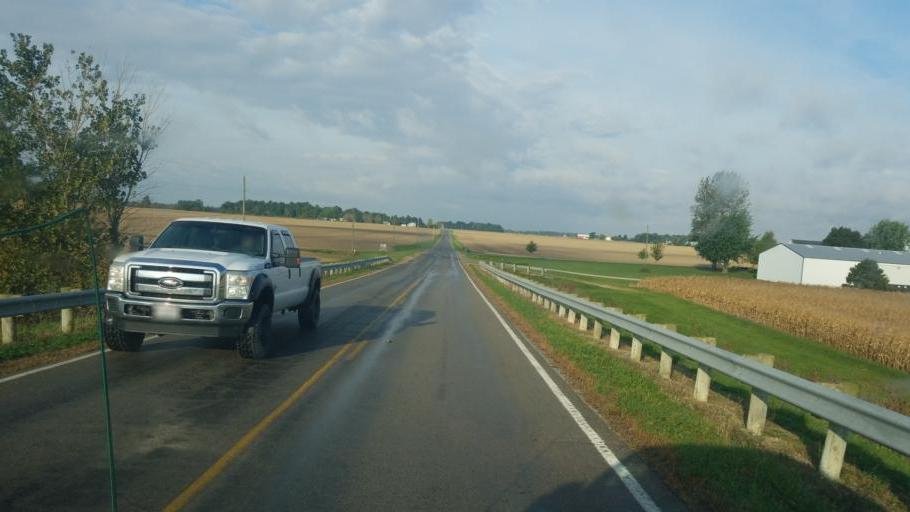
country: US
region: Ohio
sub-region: Wyandot County
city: Upper Sandusky
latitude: 40.8616
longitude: -83.3269
